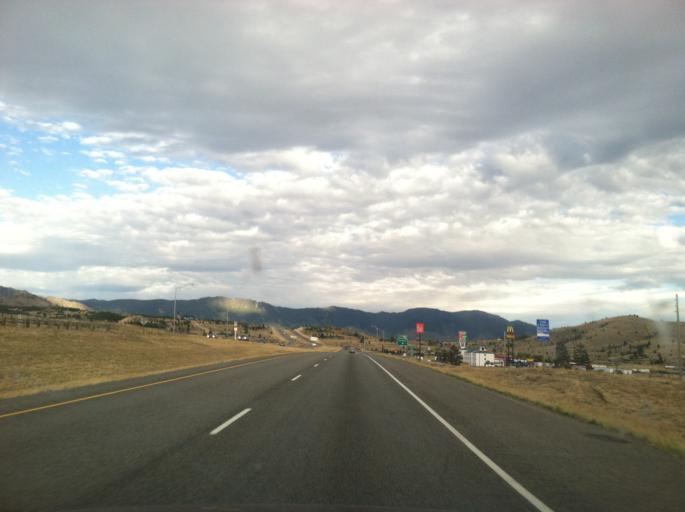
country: US
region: Montana
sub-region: Silver Bow County
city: Butte
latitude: 46.0079
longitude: -112.6211
